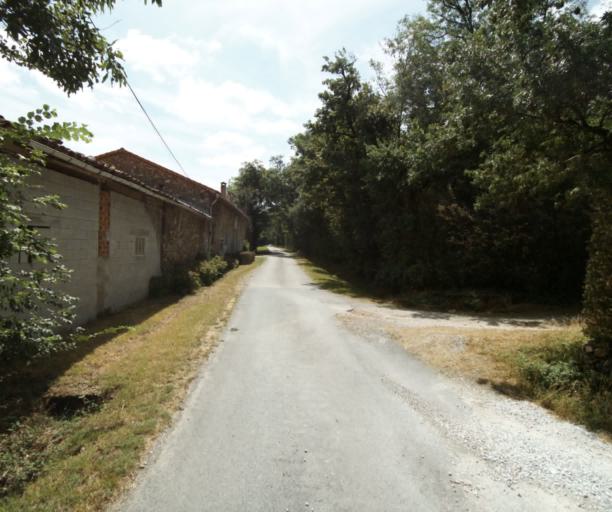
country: FR
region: Midi-Pyrenees
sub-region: Departement du Tarn
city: Dourgne
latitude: 43.4867
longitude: 2.1088
